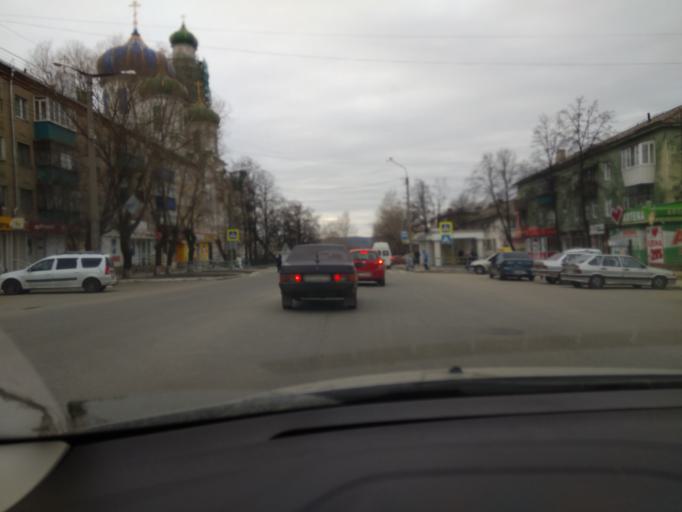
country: RU
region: Chelyabinsk
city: Kyshtym
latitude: 55.7067
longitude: 60.5515
